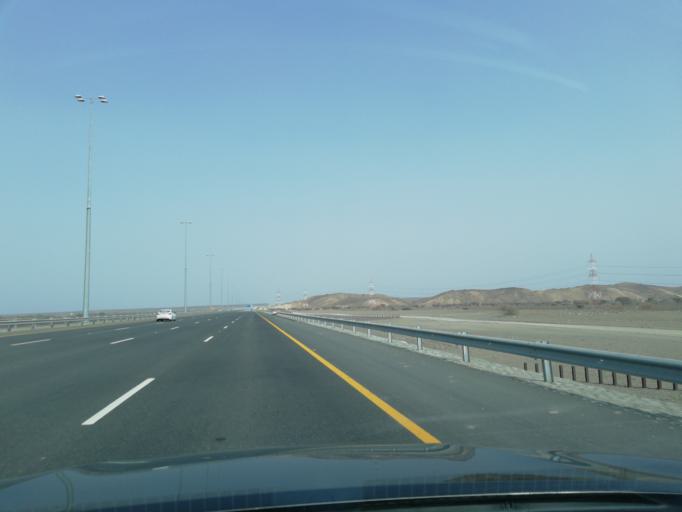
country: OM
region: Al Batinah
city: Al Sohar
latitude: 24.3039
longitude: 56.5980
